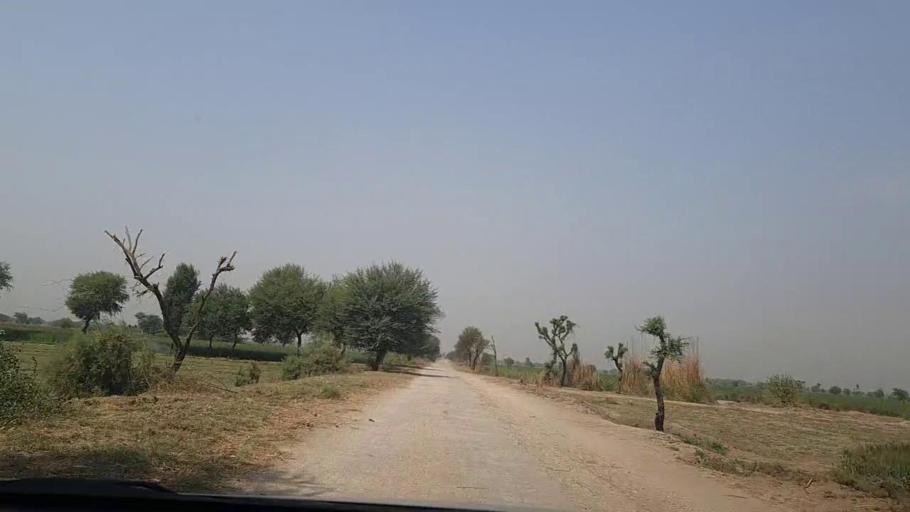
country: PK
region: Sindh
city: Mirpur Khas
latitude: 25.6116
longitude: 69.2010
